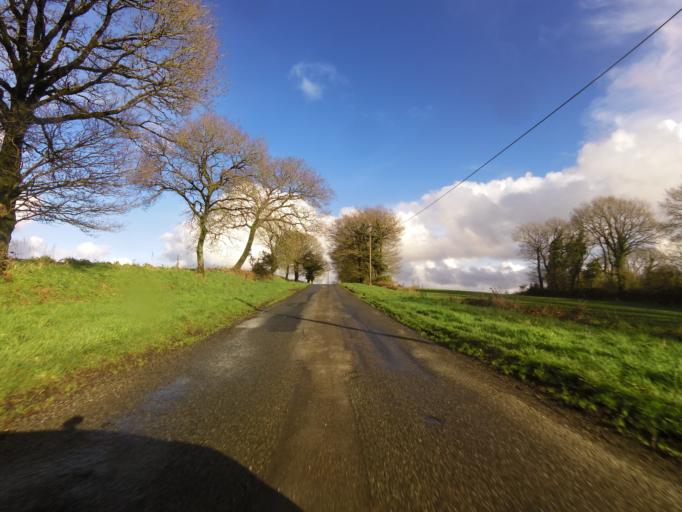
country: FR
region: Brittany
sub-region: Departement des Cotes-d'Armor
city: Gouarec
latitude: 48.1844
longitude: -3.1845
